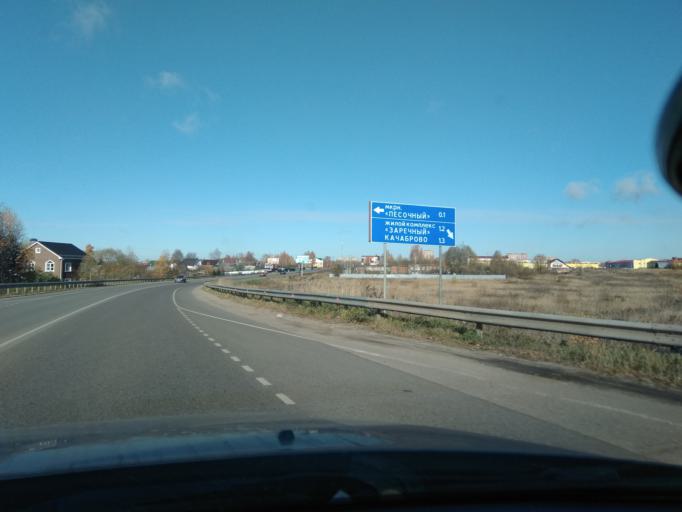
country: RU
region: Moskovskaya
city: Istra
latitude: 55.8939
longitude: 36.8640
